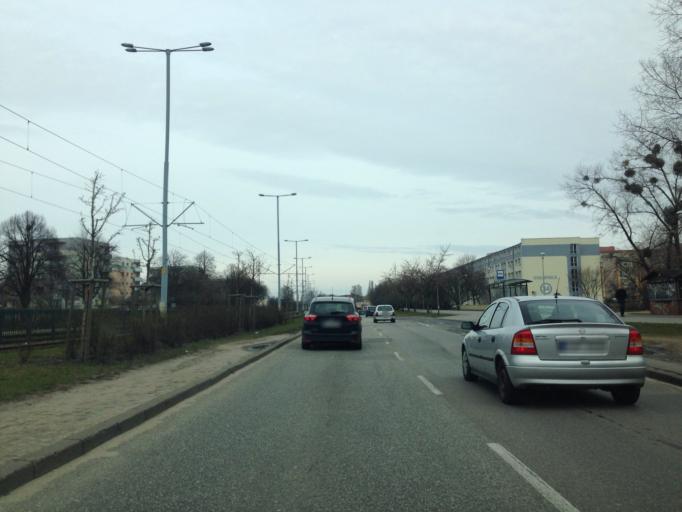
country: PL
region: Pomeranian Voivodeship
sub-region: Sopot
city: Sopot
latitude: 54.4126
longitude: 18.5880
